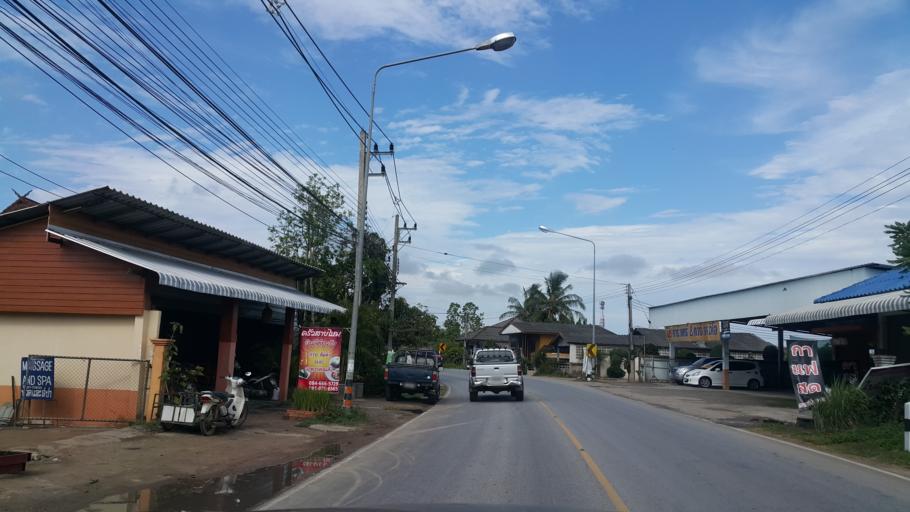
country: TH
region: Chiang Rai
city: Chiang Rai
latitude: 19.9124
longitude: 99.8838
